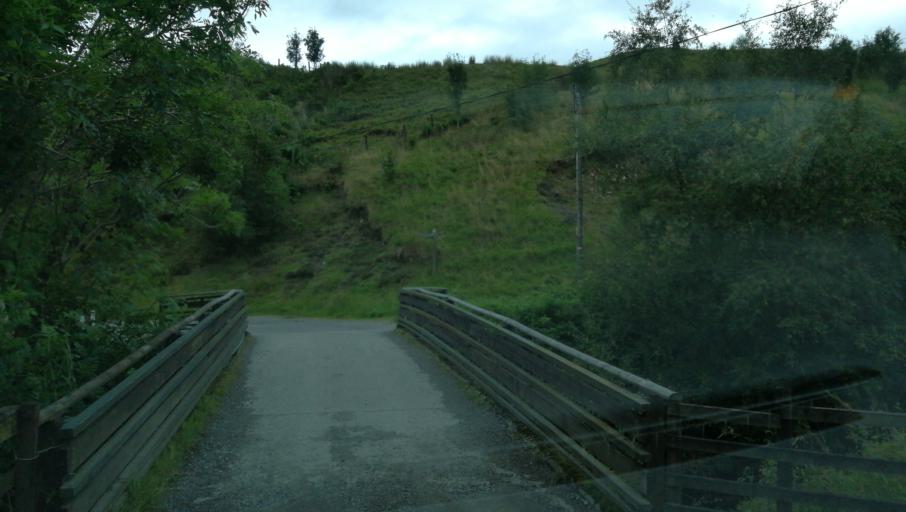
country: GB
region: Scotland
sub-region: Argyll and Bute
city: Garelochhead
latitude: 56.4248
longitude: -4.6706
